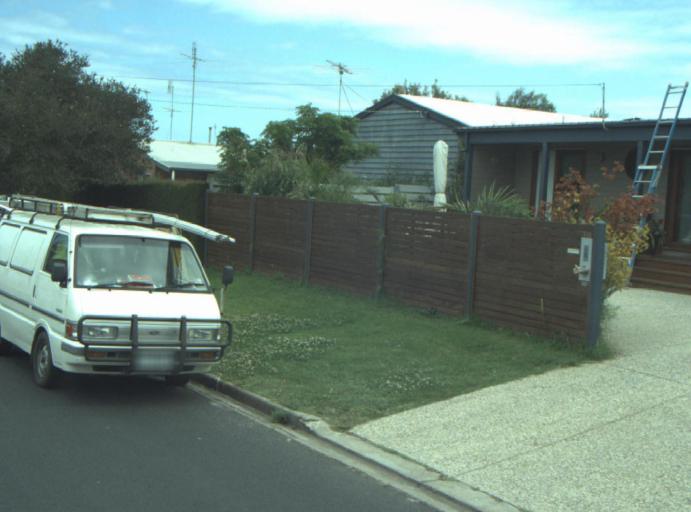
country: AU
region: Victoria
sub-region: Greater Geelong
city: Leopold
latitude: -38.2666
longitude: 144.5430
